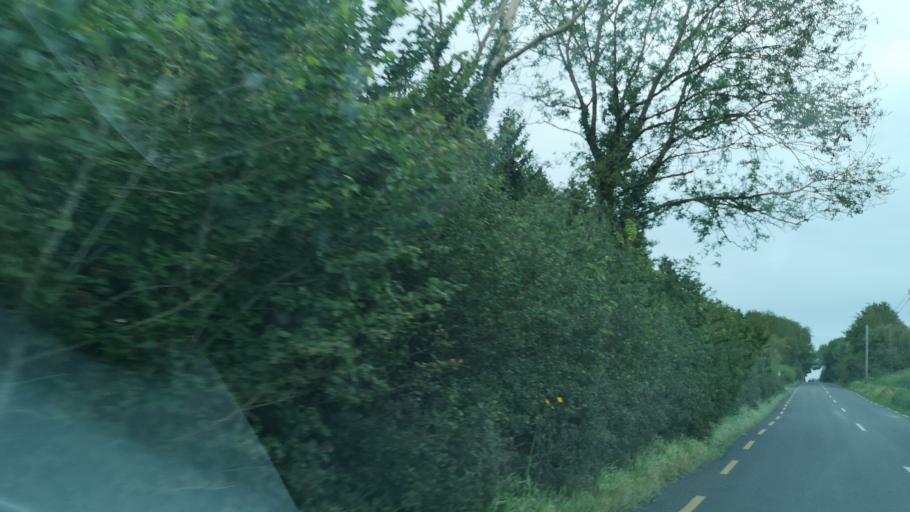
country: IE
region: Leinster
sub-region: Uibh Fhaili
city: Ferbane
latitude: 53.2297
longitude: -7.7820
